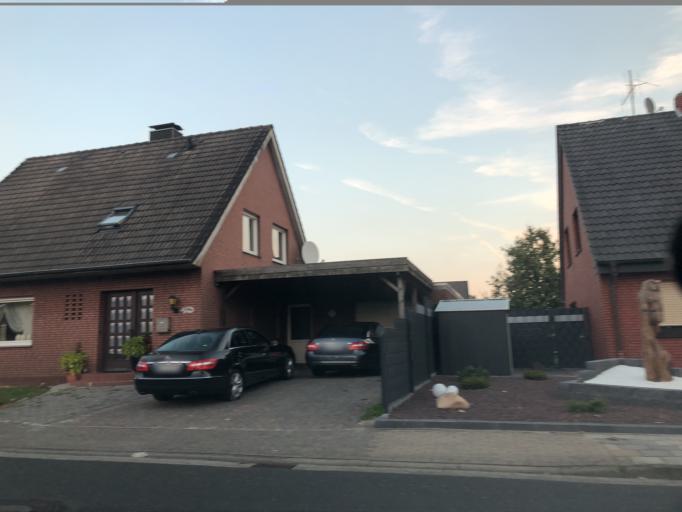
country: DE
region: Lower Saxony
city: Papenburg
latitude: 53.0715
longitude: 7.4318
